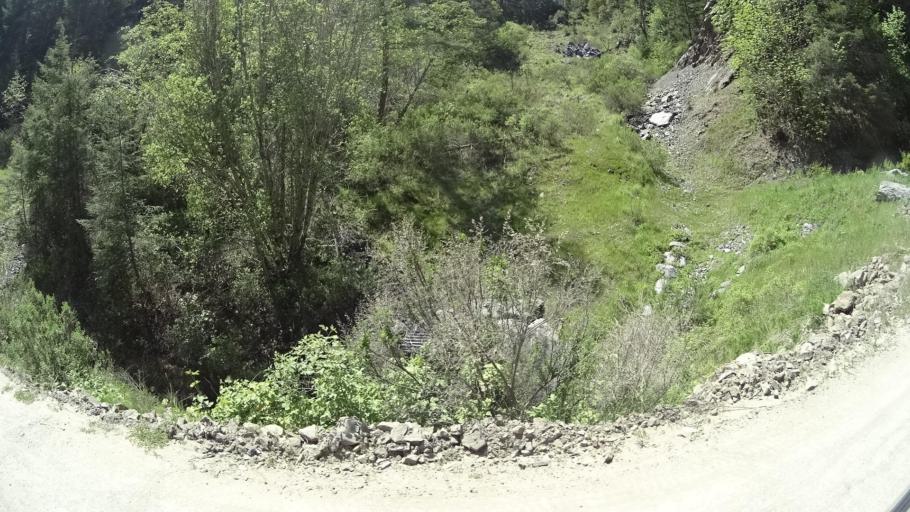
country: US
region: California
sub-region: Humboldt County
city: Redway
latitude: 40.1978
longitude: -123.5269
